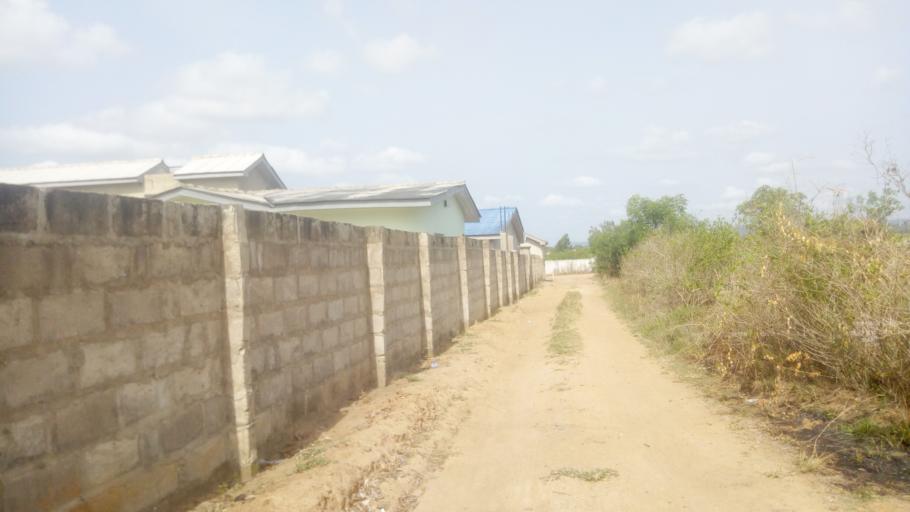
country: GH
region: Central
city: Winneba
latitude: 5.3783
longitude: -0.6279
